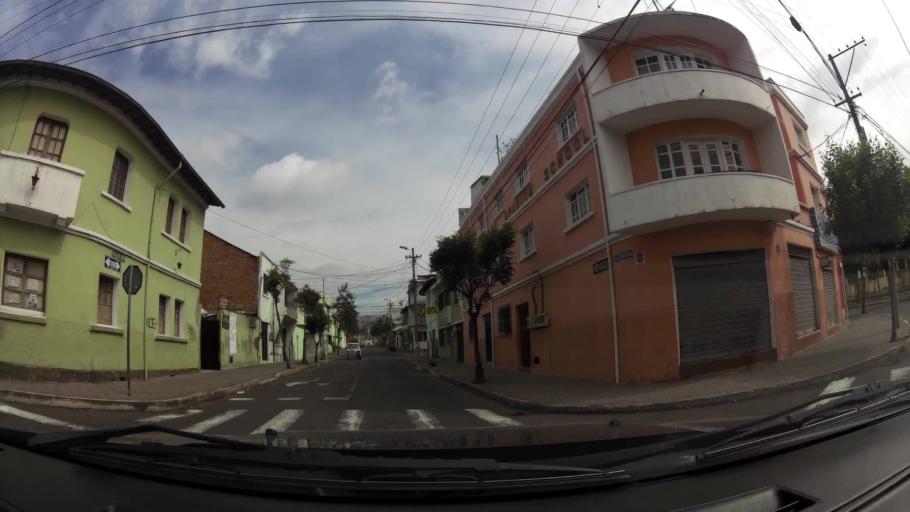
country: EC
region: Pichincha
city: Quito
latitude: -0.2149
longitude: -78.4890
